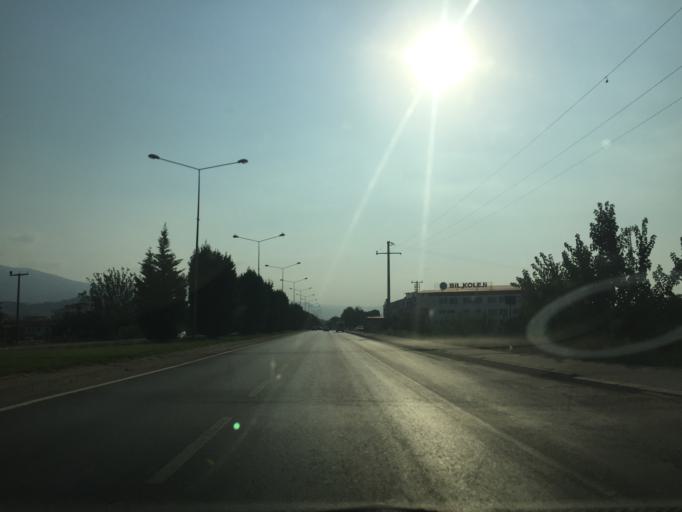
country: TR
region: Manisa
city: Salihli
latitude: 38.4919
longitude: 28.1672
